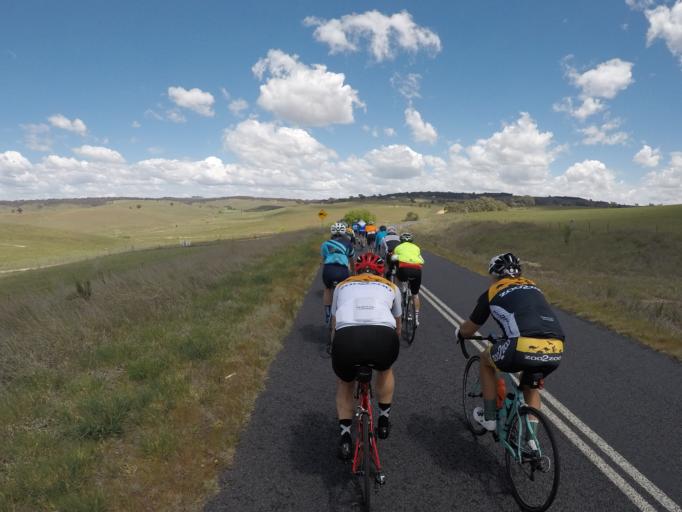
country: AU
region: New South Wales
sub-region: Bathurst Regional
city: Perthville
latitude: -33.5673
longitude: 149.4142
